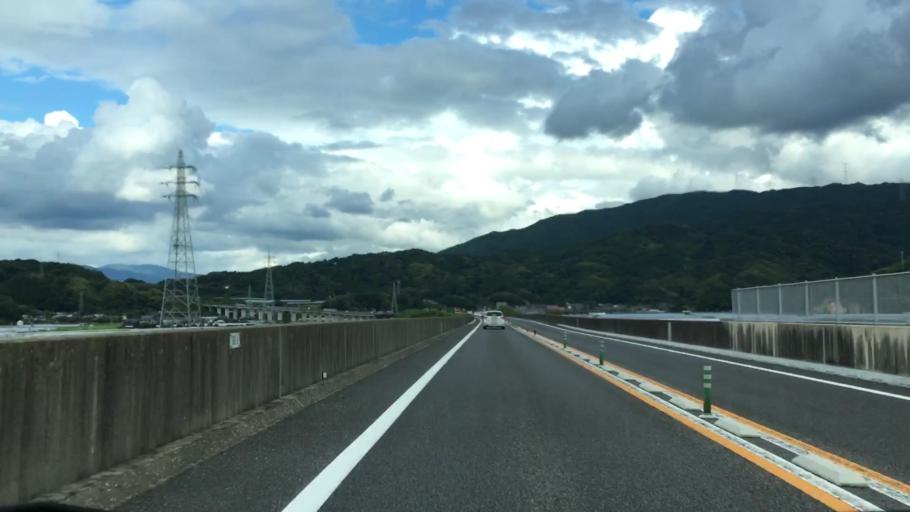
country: JP
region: Saga Prefecture
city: Karatsu
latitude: 33.4150
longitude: 130.0126
